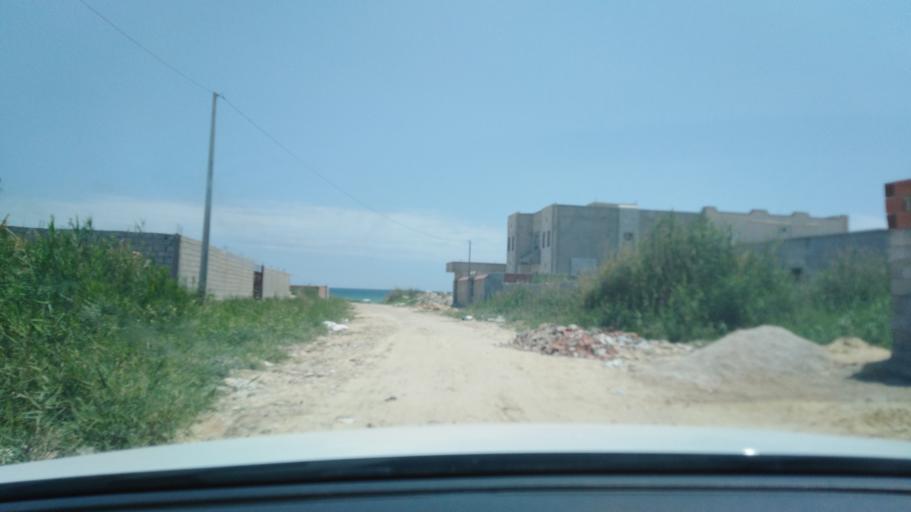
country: TN
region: Qabis
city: Gabes
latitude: 33.9465
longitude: 10.0736
